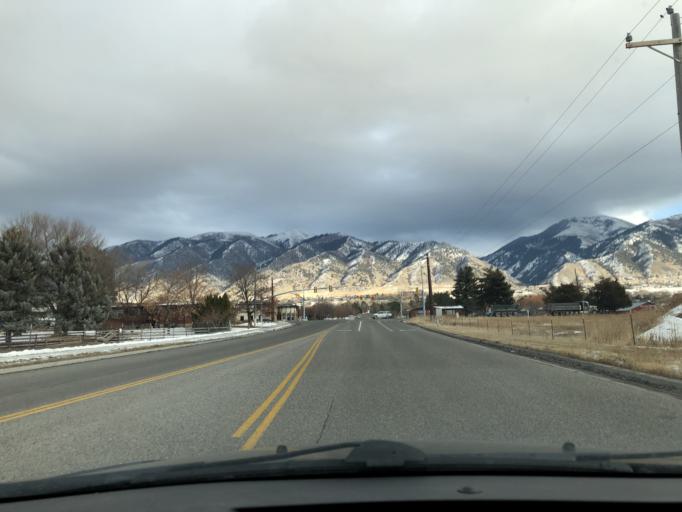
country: US
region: Utah
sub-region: Cache County
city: Providence
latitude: 41.7027
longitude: -111.8365
